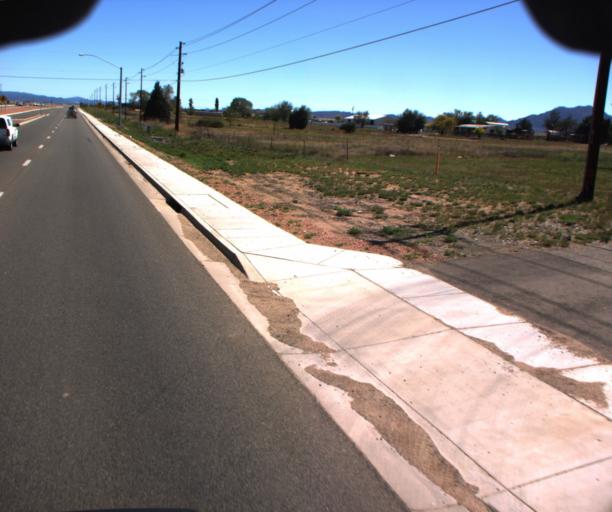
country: US
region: Arizona
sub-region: Yavapai County
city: Chino Valley
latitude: 34.7246
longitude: -112.4539
